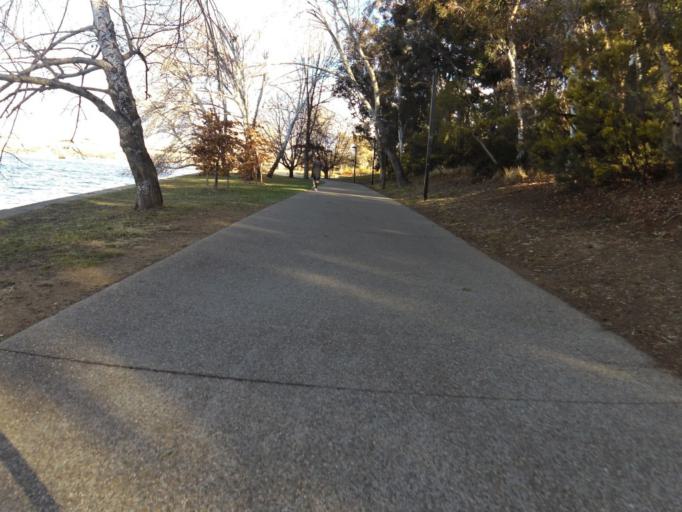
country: AU
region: Australian Capital Territory
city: Forrest
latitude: -35.3000
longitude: 149.1385
